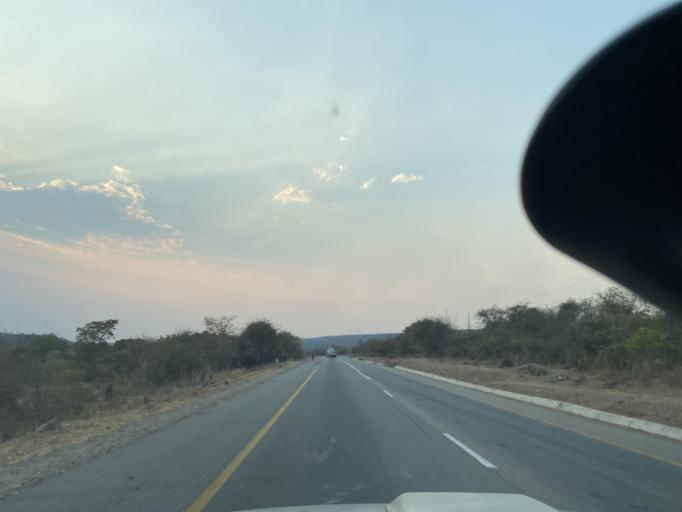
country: ZM
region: Lusaka
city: Kafue
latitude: -15.9010
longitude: 28.3459
